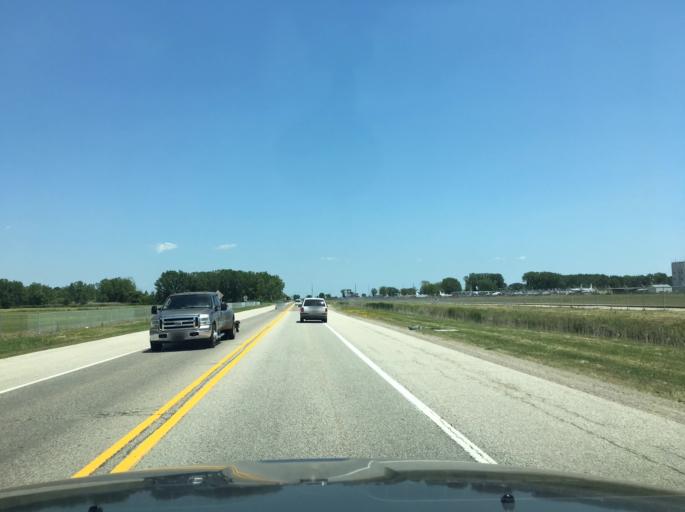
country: US
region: Michigan
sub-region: Macomb County
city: Mount Clemens
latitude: 42.6304
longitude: -82.8360
